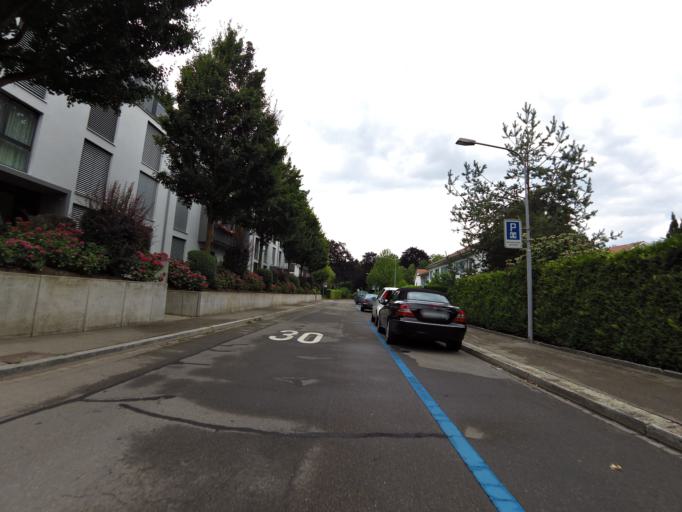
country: CH
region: Zurich
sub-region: Bezirk Zuerich
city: Zuerich (Kreis 11)
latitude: 47.4128
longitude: 8.5248
